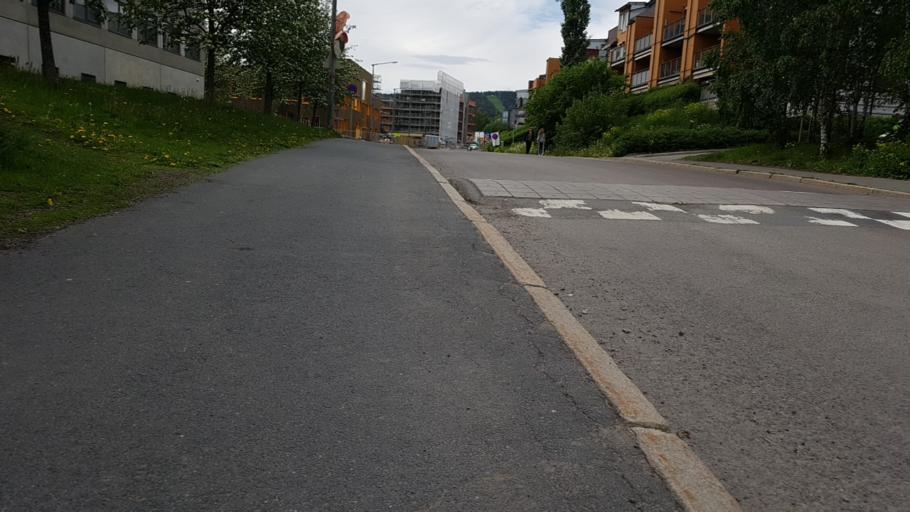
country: NO
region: Oslo
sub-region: Oslo
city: Oslo
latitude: 59.9367
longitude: 10.8309
